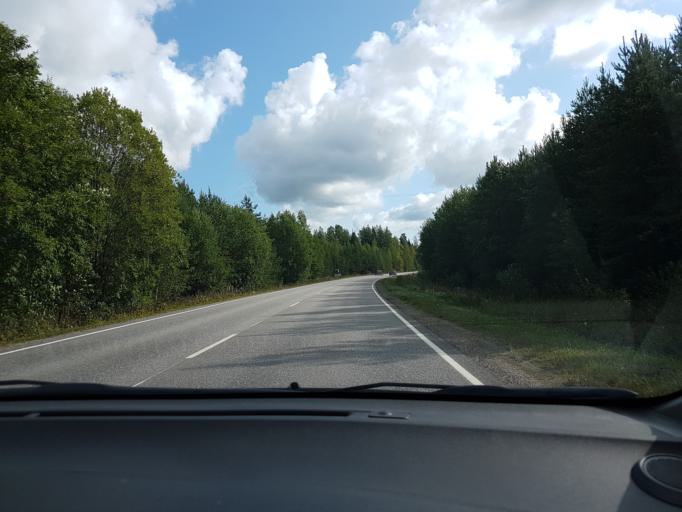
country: FI
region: Uusimaa
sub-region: Helsinki
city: Sibbo
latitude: 60.4747
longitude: 25.2149
